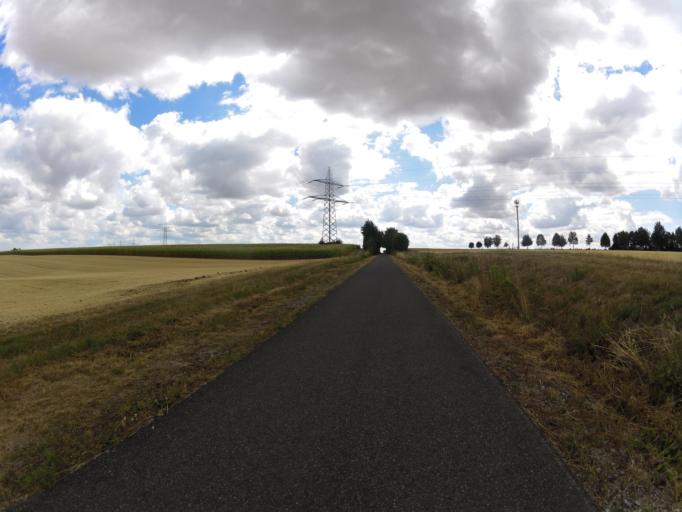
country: DE
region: Bavaria
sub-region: Regierungsbezirk Unterfranken
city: Sonderhofen
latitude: 49.5864
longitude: 10.0083
